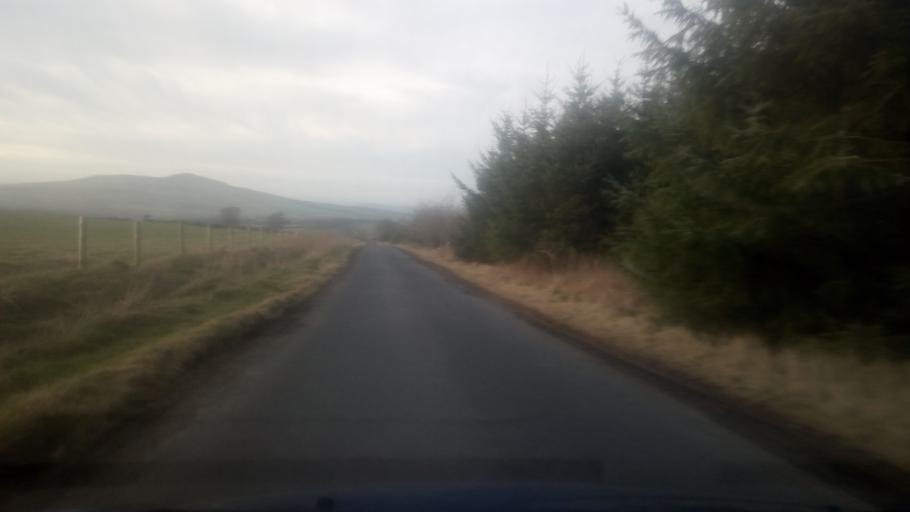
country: GB
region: Scotland
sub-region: The Scottish Borders
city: Jedburgh
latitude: 55.3997
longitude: -2.5960
